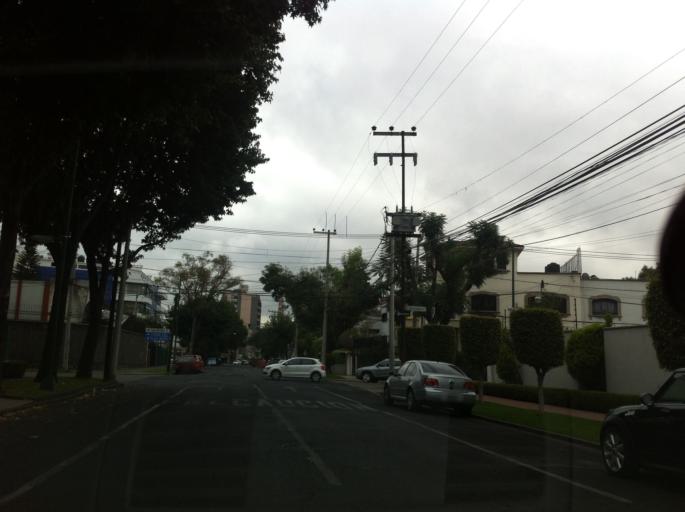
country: MX
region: Mexico City
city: Colonia del Valle
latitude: 19.3853
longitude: -99.1739
